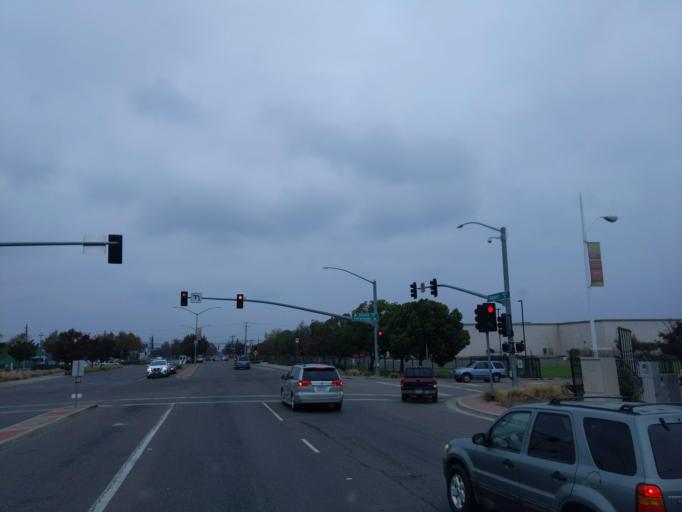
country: US
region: California
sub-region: San Joaquin County
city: Kennedy
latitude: 37.9392
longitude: -121.2699
